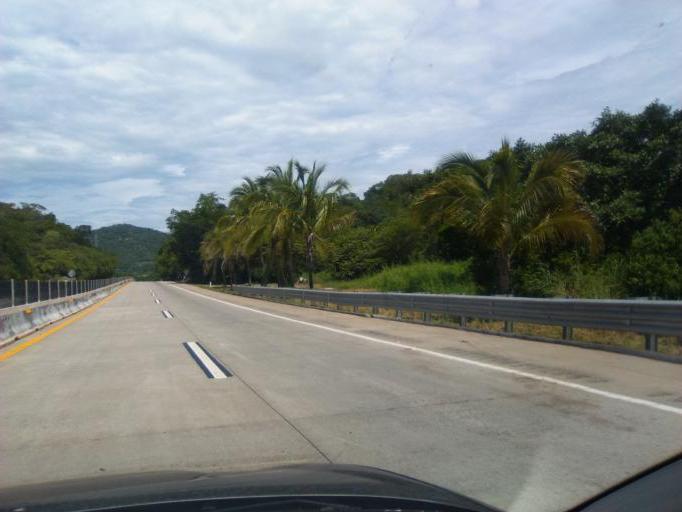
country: MX
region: Guerrero
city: Tierra Colorada
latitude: 17.1332
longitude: -99.5572
